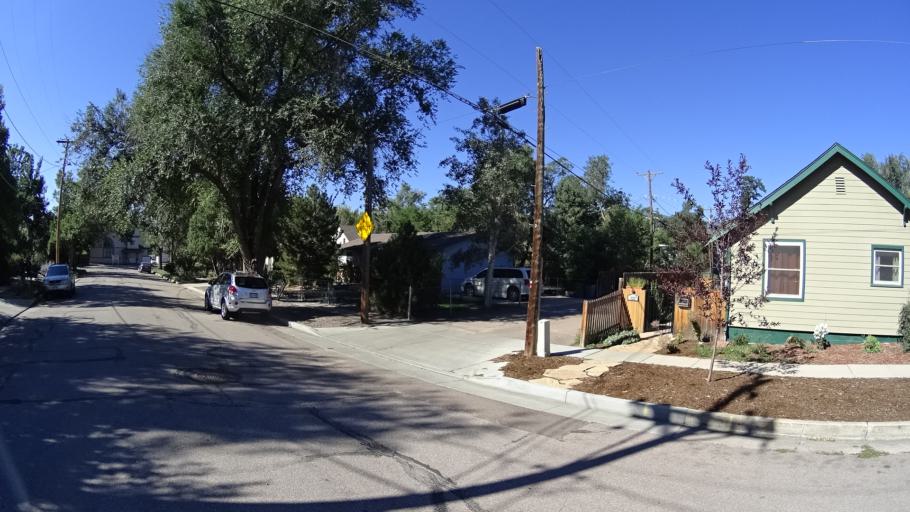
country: US
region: Colorado
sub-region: El Paso County
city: Colorado Springs
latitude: 38.8414
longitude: -104.8151
